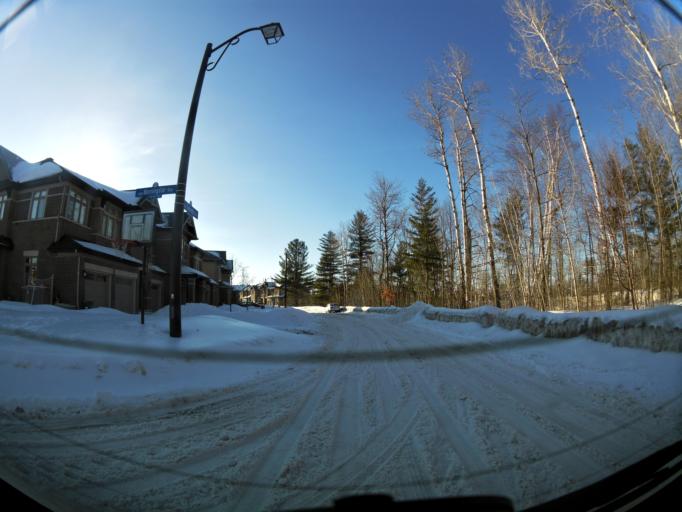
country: CA
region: Ontario
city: Ottawa
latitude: 45.4343
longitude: -75.5171
